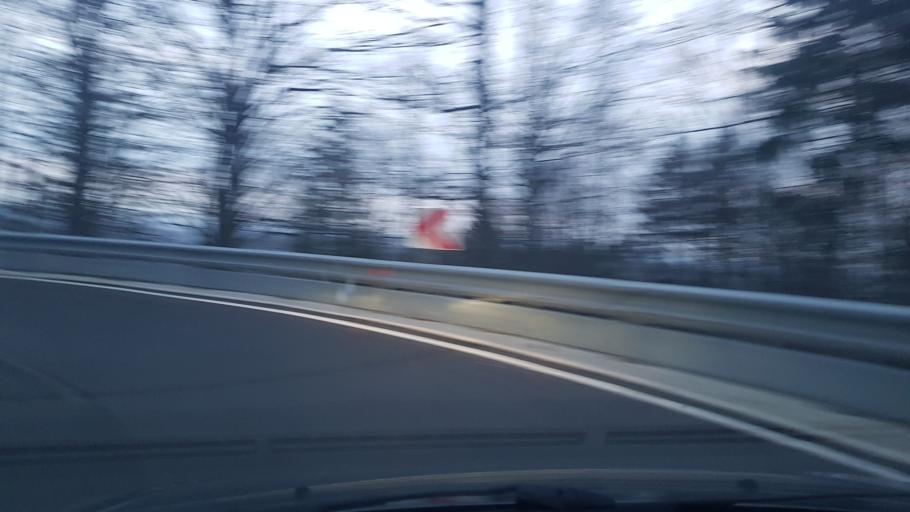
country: SI
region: Idrija
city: Idrija
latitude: 45.9217
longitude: 14.0464
